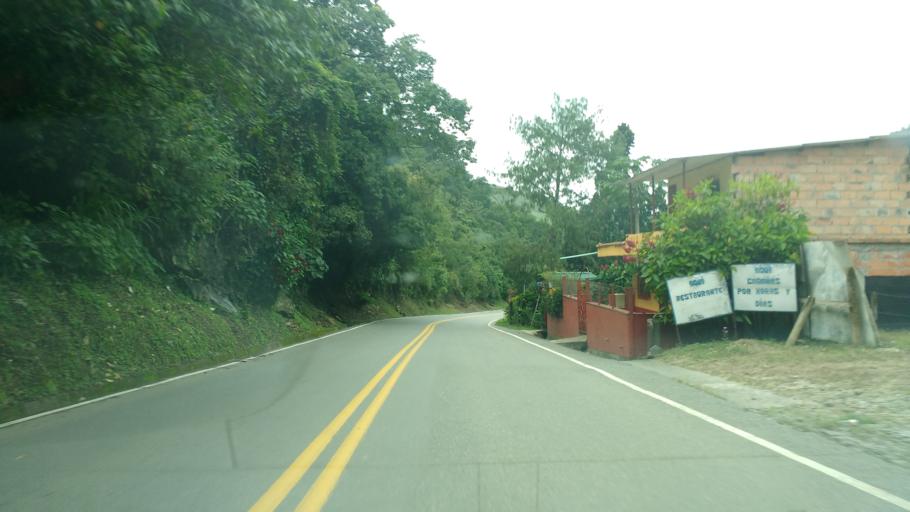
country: CO
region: Antioquia
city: Amaga
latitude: 6.0606
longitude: -75.7300
